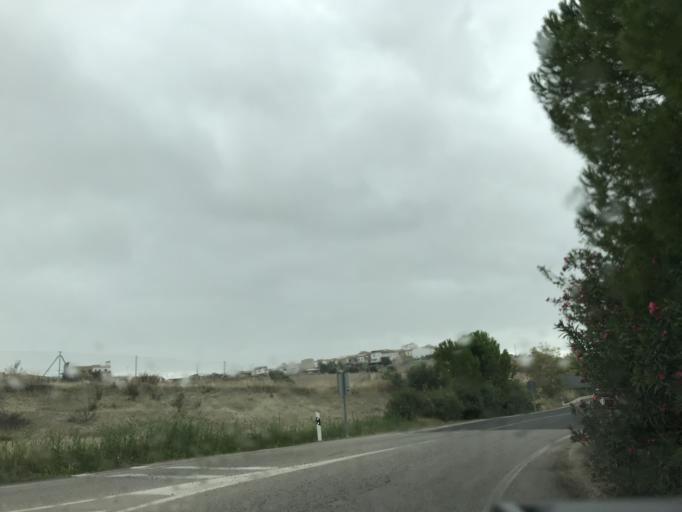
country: ES
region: Andalusia
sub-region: Provincia de Jaen
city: Peal de Becerro
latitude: 37.9194
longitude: -3.1222
